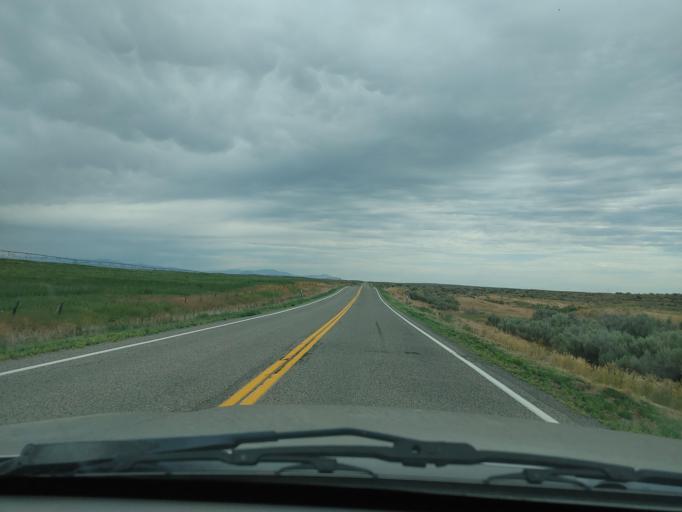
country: US
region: Idaho
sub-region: Lincoln County
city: Shoshone
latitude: 43.0608
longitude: -114.1271
